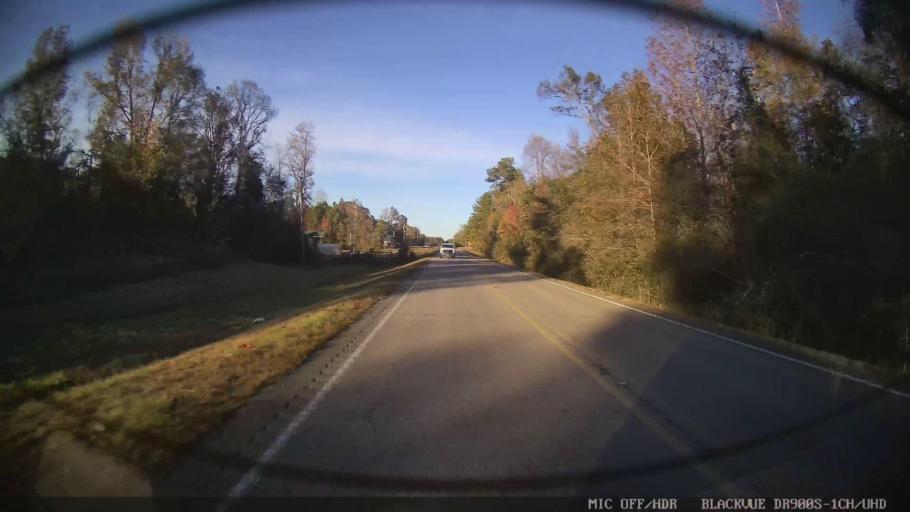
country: US
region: Mississippi
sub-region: Lamar County
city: Lumberton
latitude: 31.0651
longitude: -89.4240
